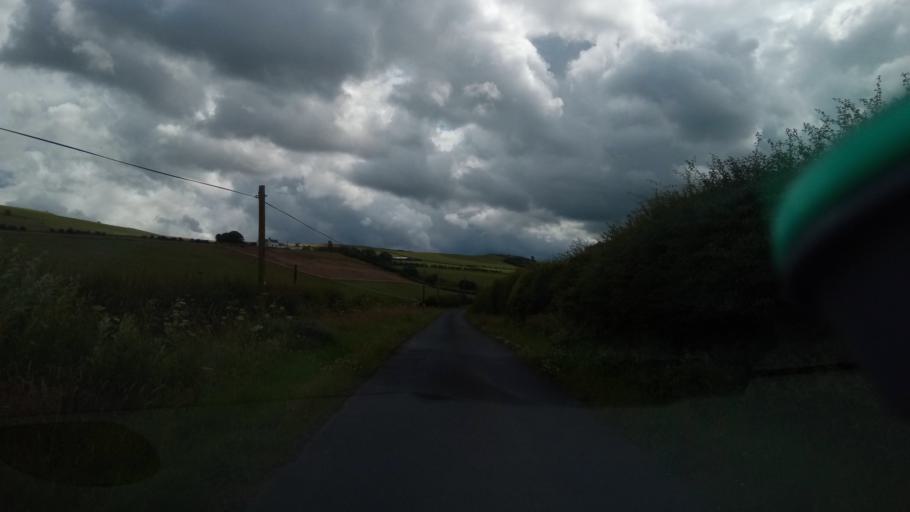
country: GB
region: Scotland
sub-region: The Scottish Borders
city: Kelso
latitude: 55.4932
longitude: -2.4280
